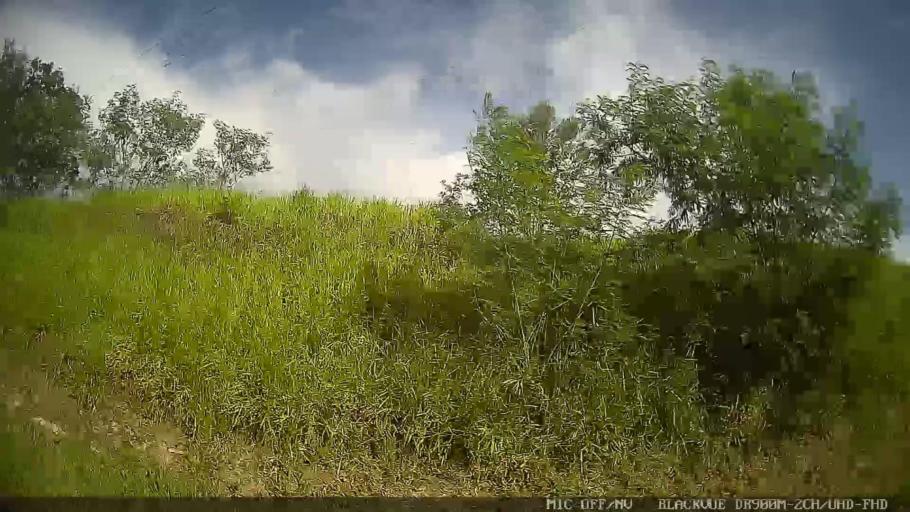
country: BR
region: Sao Paulo
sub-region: Tiete
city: Tiete
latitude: -23.0981
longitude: -47.6898
